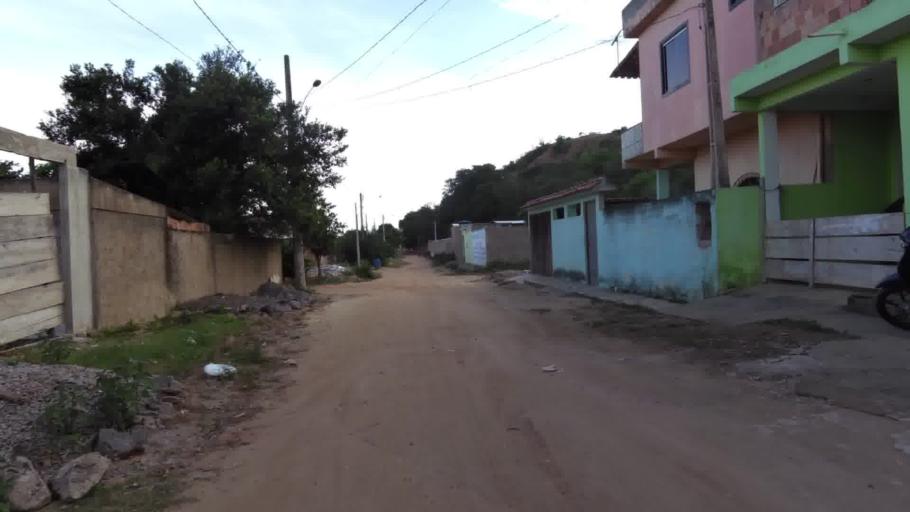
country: BR
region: Espirito Santo
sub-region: Piuma
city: Piuma
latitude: -20.8397
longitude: -40.7481
